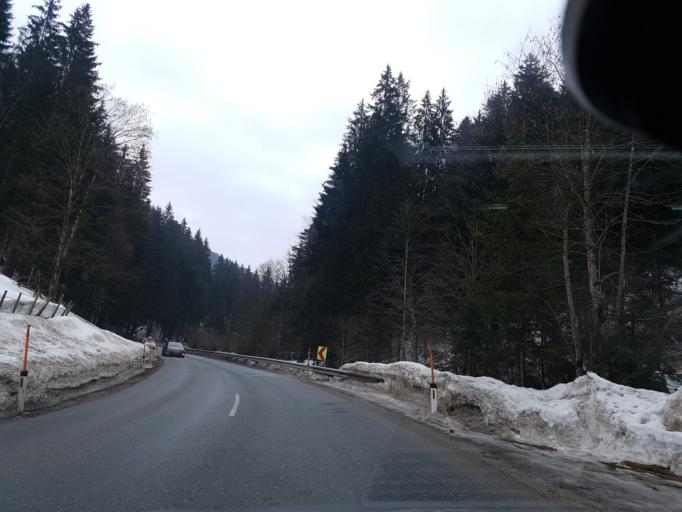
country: AT
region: Tyrol
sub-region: Politischer Bezirk Kufstein
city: Worgl
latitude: 47.4635
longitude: 12.0893
